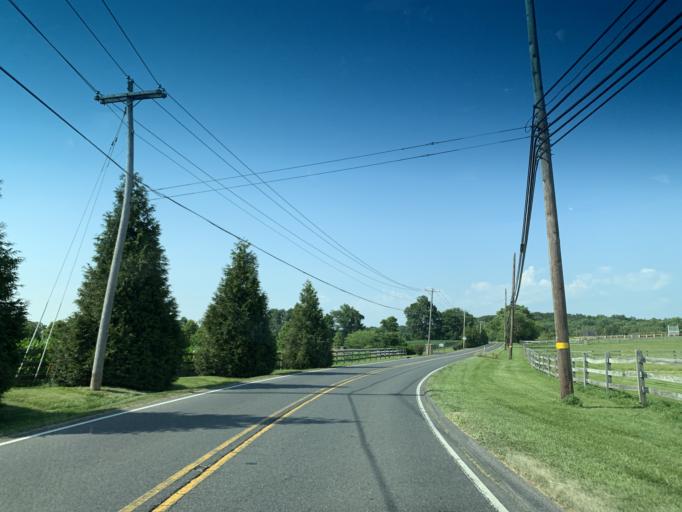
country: US
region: Maryland
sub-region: Montgomery County
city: Poolesville
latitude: 39.1616
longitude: -77.4191
